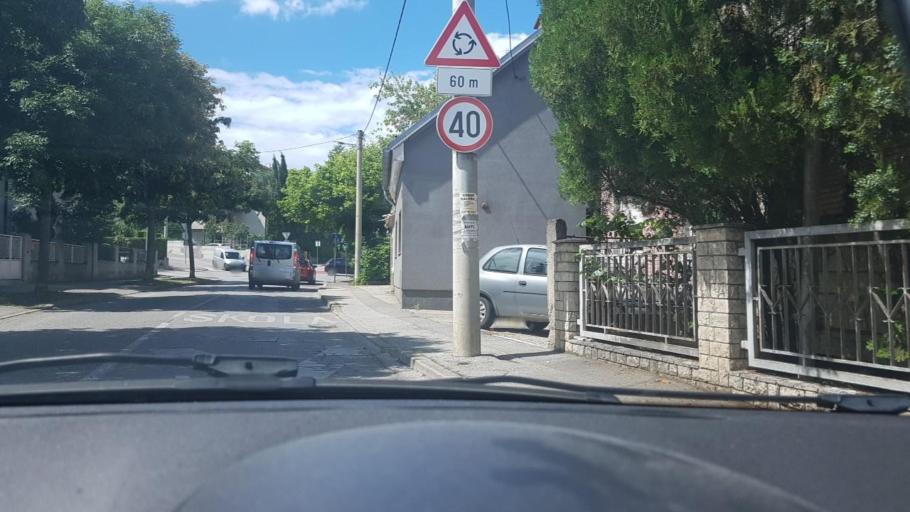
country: HR
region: Grad Zagreb
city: Zagreb
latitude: 45.8266
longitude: 16.0071
